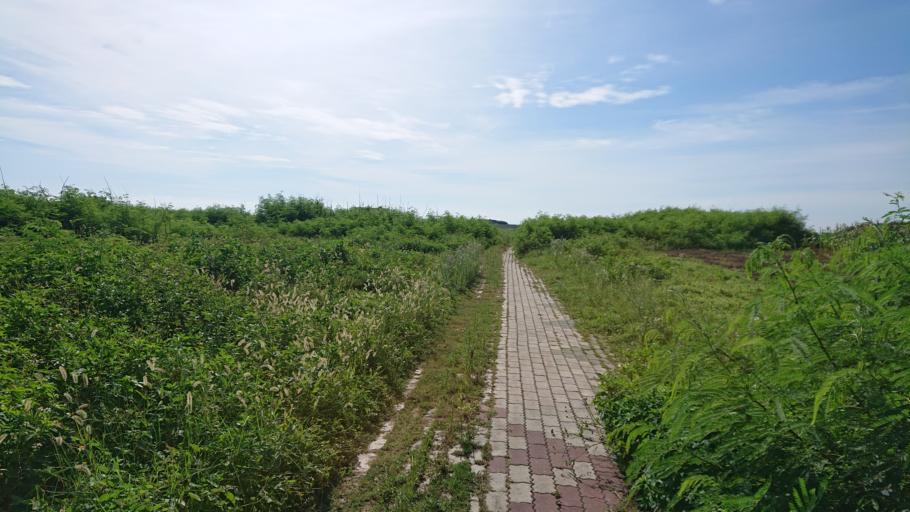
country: TW
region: Taiwan
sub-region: Penghu
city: Ma-kung
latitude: 23.6510
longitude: 119.5214
